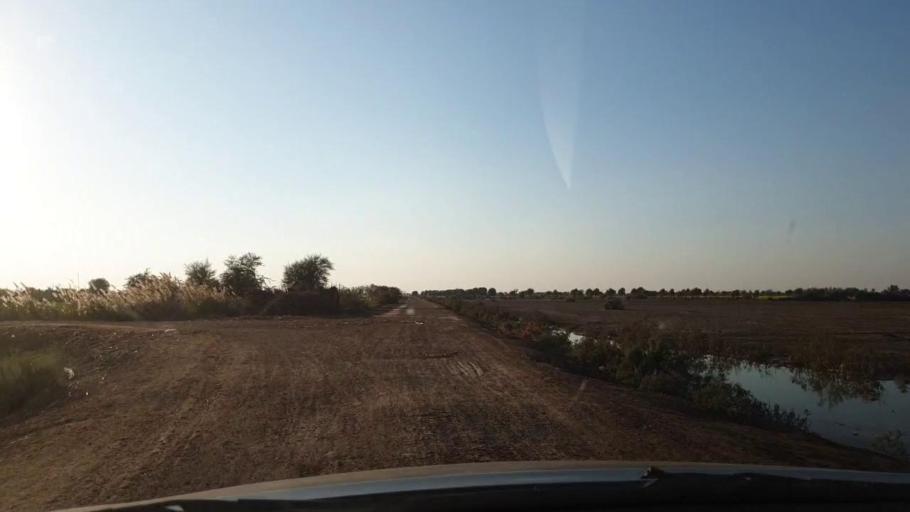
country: PK
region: Sindh
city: Tando Mittha Khan
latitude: 25.8321
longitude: 69.1704
